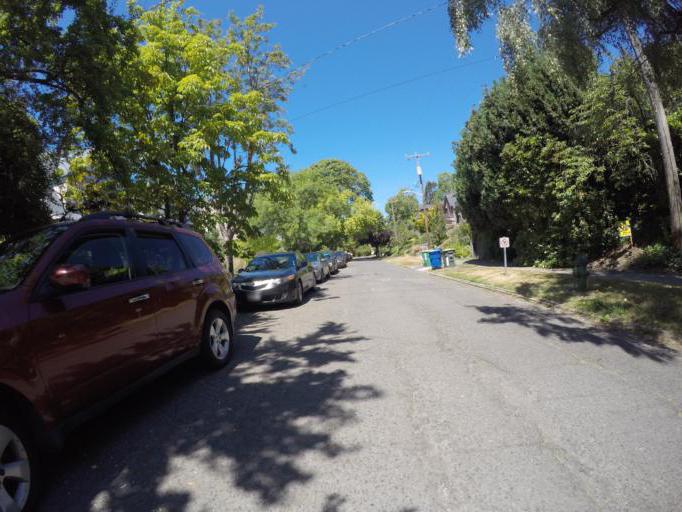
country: US
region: Washington
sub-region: King County
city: Seattle
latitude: 47.6275
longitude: -122.3167
